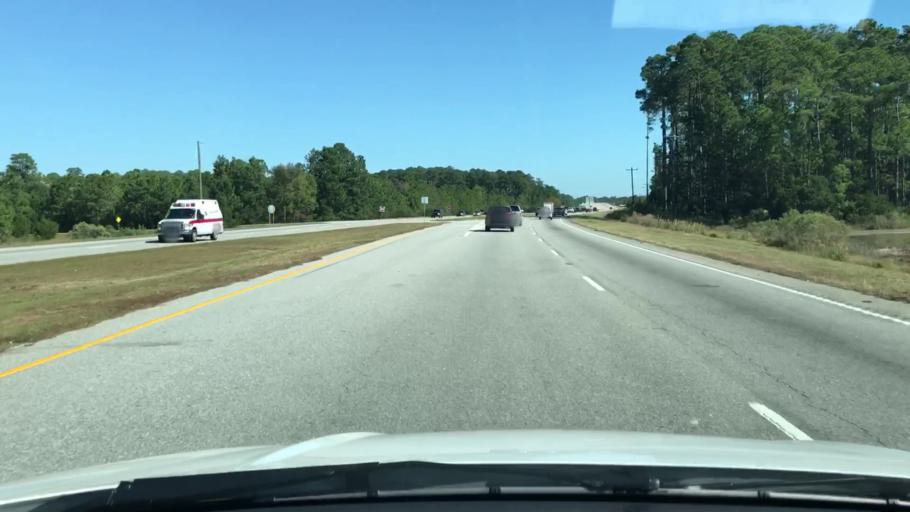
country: US
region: South Carolina
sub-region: Beaufort County
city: Laurel Bay
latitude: 32.3735
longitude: -80.8467
